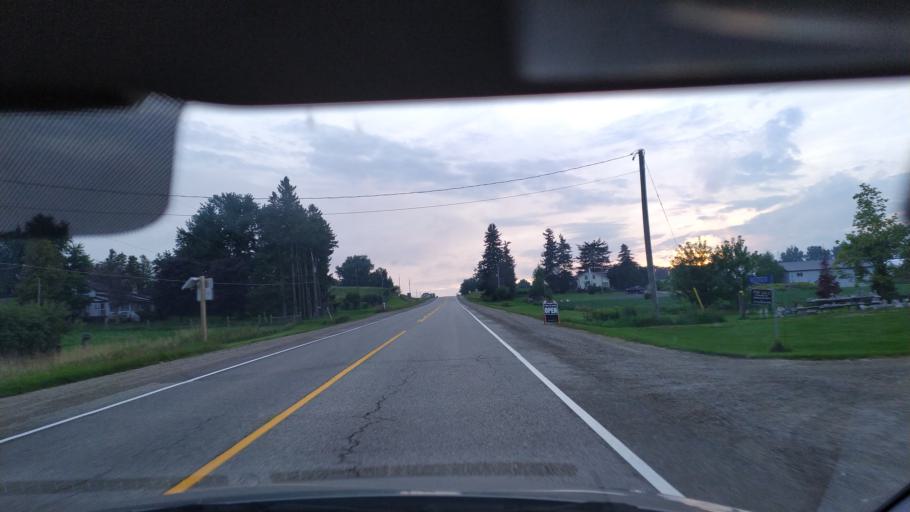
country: CA
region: Ontario
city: Kitchener
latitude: 43.3091
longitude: -80.5843
